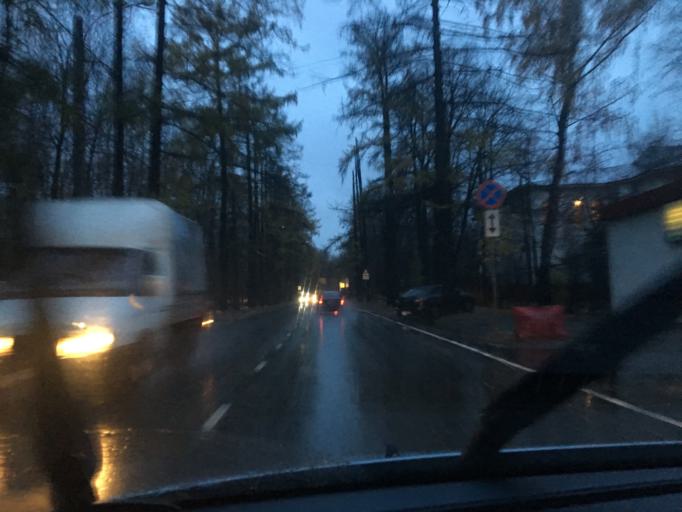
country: RU
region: Moscow
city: Sokol'niki
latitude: 55.7995
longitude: 37.6576
